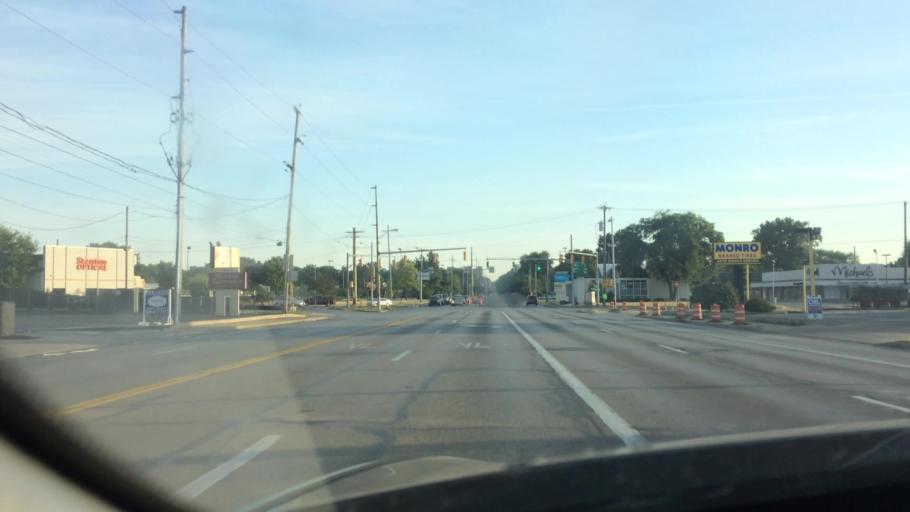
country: US
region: Ohio
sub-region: Lucas County
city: Ottawa Hills
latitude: 41.6982
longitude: -83.6449
